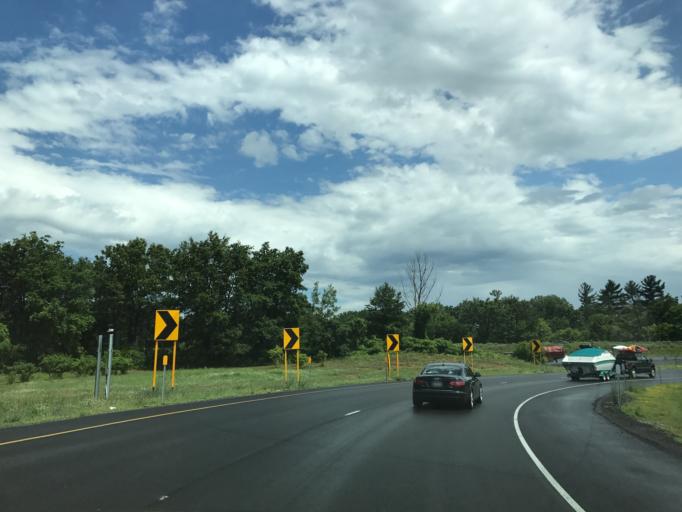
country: US
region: New York
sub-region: Albany County
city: McKownville
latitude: 42.7007
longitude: -73.8467
